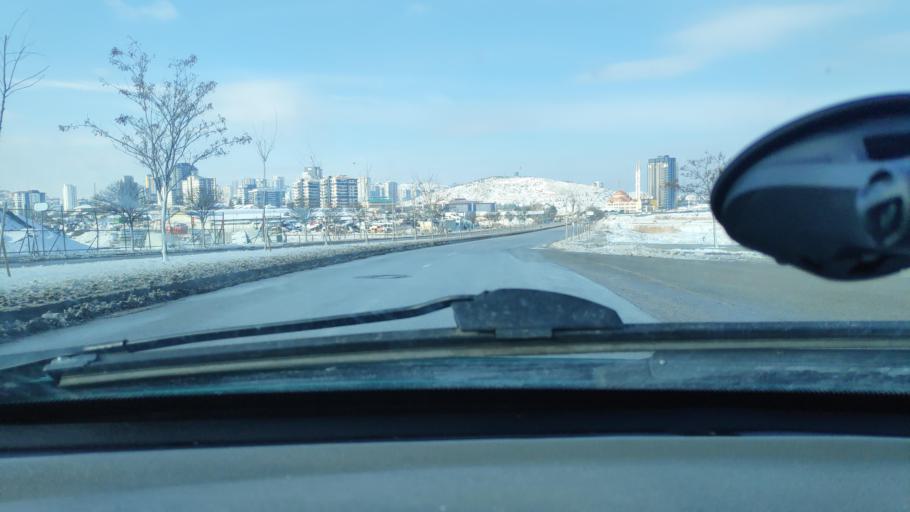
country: TR
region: Ankara
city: Ankara
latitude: 40.0154
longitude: 32.8356
